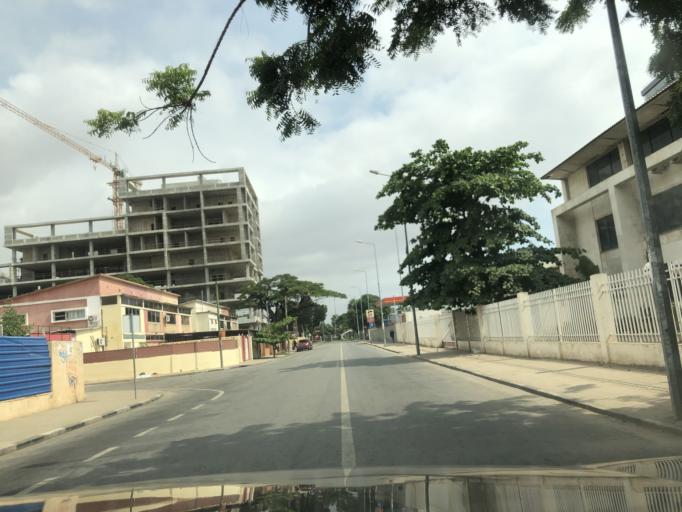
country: AO
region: Luanda
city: Luanda
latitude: -8.8255
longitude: 13.2456
